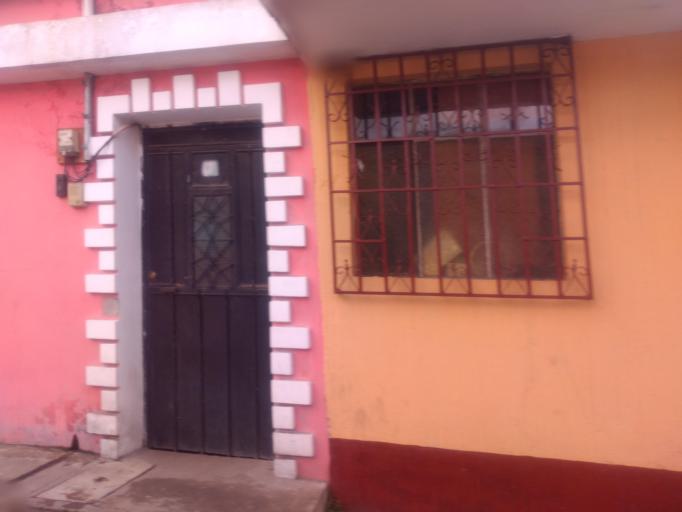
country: GT
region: Quetzaltenango
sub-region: Municipio de La Esperanza
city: La Esperanza
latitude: 14.8707
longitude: -91.5607
